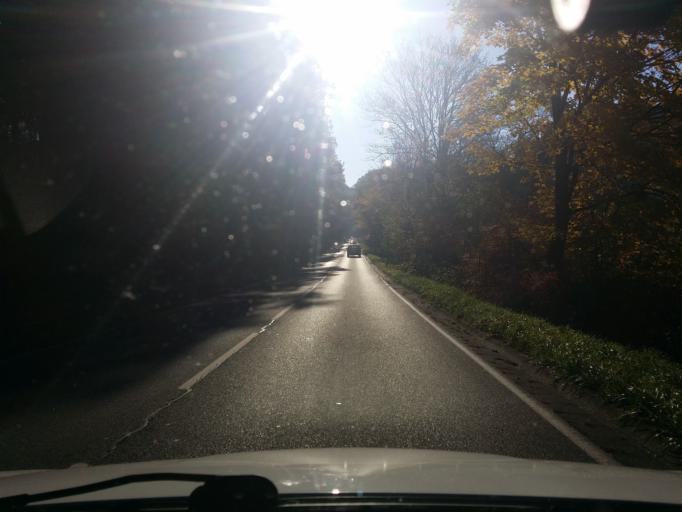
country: DE
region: Hesse
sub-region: Regierungsbezirk Darmstadt
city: Niedernhausen
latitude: 50.1788
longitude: 8.2966
